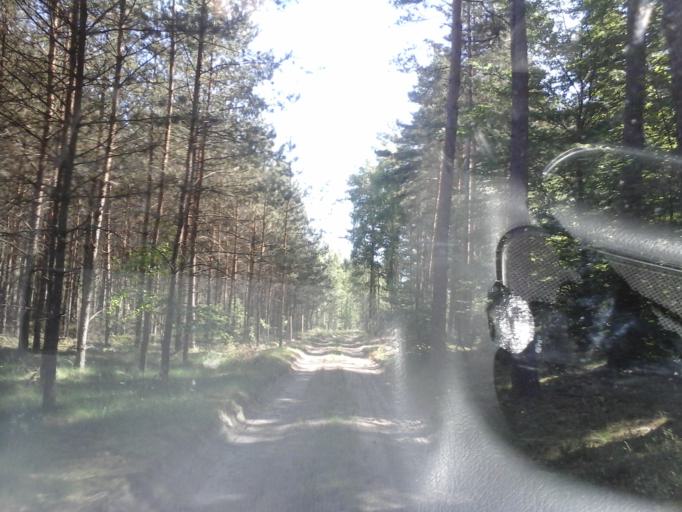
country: PL
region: West Pomeranian Voivodeship
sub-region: Powiat choszczenski
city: Drawno
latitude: 53.1439
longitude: 15.8843
